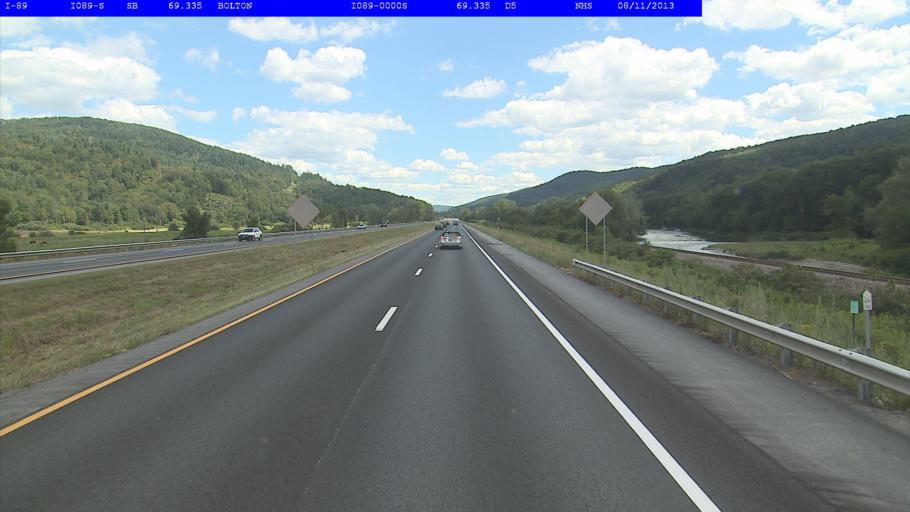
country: US
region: Vermont
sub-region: Washington County
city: Waterbury
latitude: 44.3664
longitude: -72.8558
